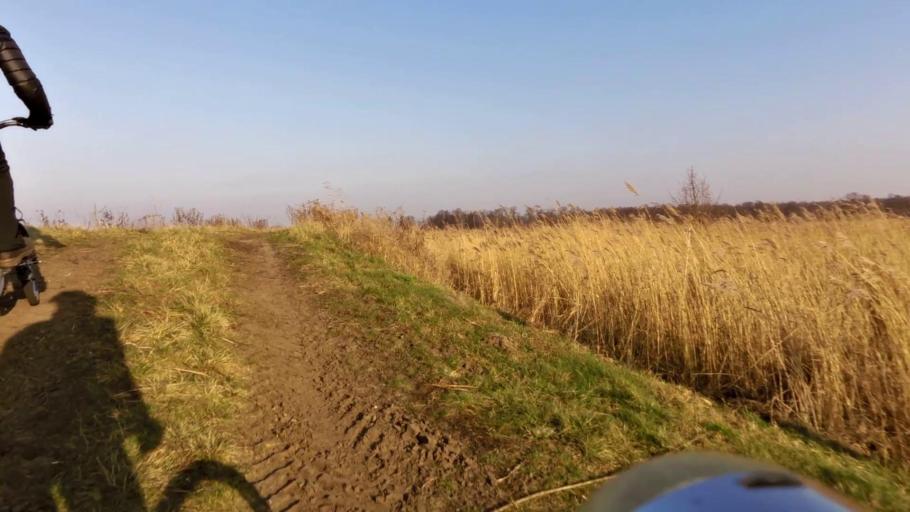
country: PL
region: West Pomeranian Voivodeship
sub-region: Powiat kamienski
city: Wolin
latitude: 53.7566
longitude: 14.5870
